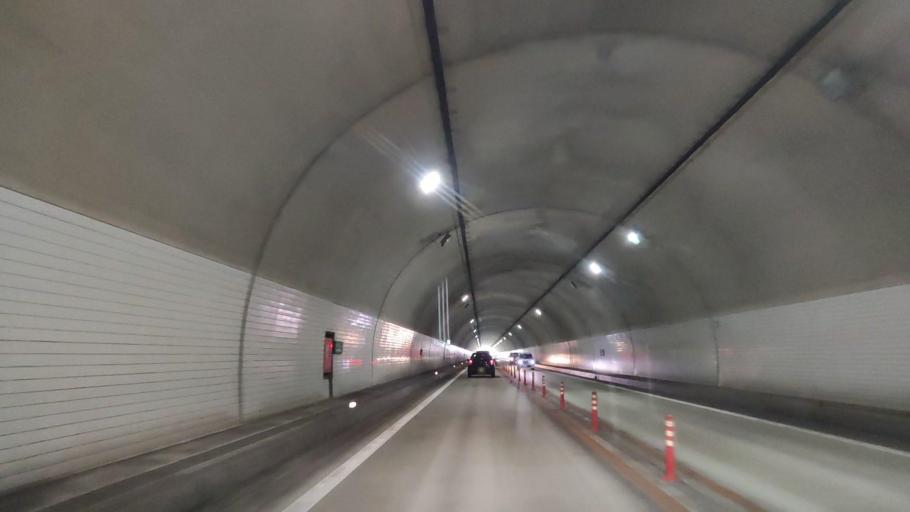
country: JP
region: Akita
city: Takanosu
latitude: 40.2216
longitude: 140.4299
